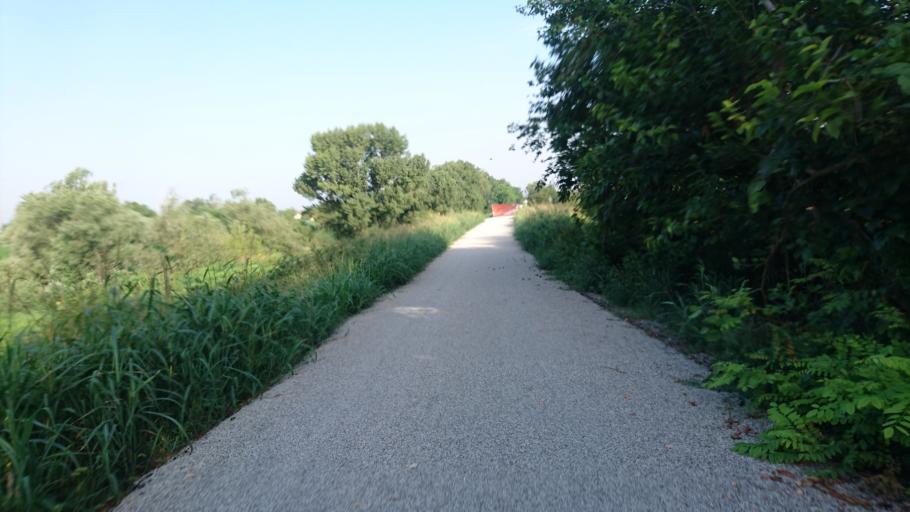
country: IT
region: Veneto
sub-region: Provincia di Padova
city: Mejaniga
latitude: 45.4418
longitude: 11.9065
